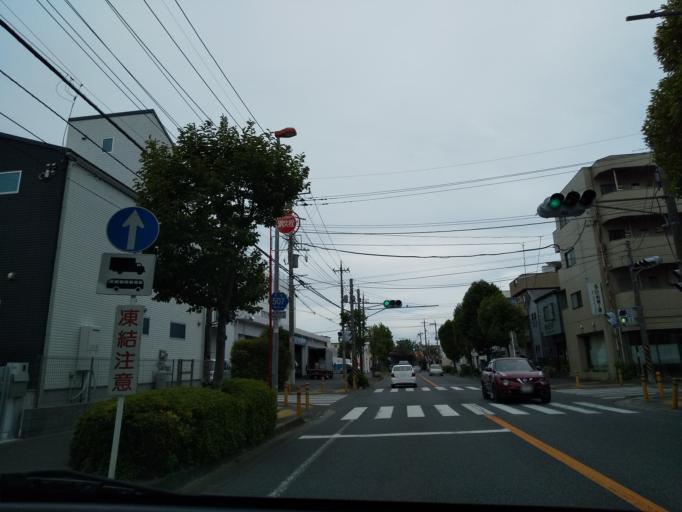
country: JP
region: Kanagawa
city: Zama
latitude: 35.5150
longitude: 139.4065
